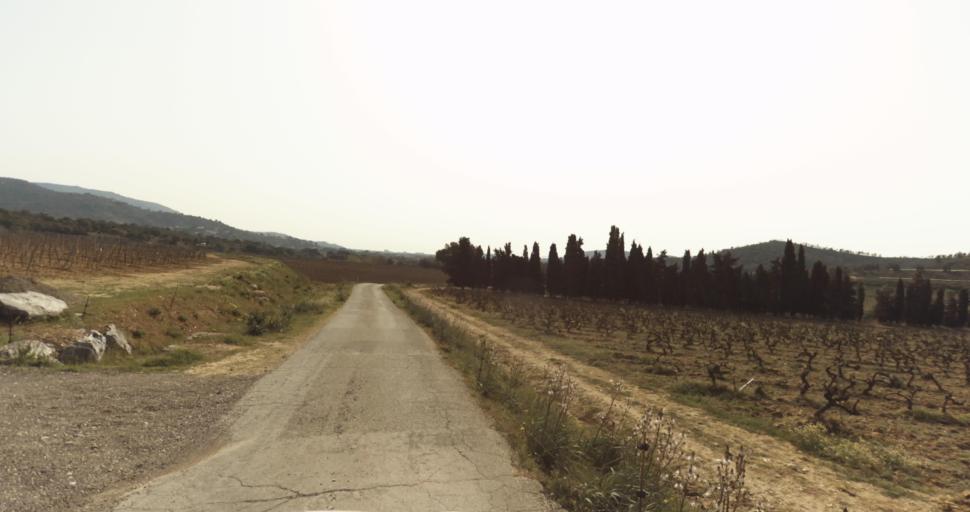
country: FR
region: Provence-Alpes-Cote d'Azur
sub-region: Departement du Var
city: Bormes-les-Mimosas
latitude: 43.1448
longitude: 6.3081
